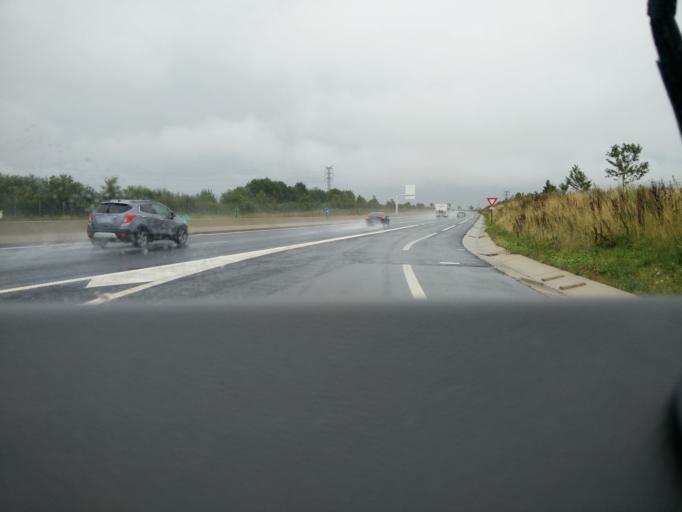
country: FR
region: Nord-Pas-de-Calais
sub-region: Departement du Pas-de-Calais
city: Marconnelle
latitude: 50.3696
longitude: 1.9435
